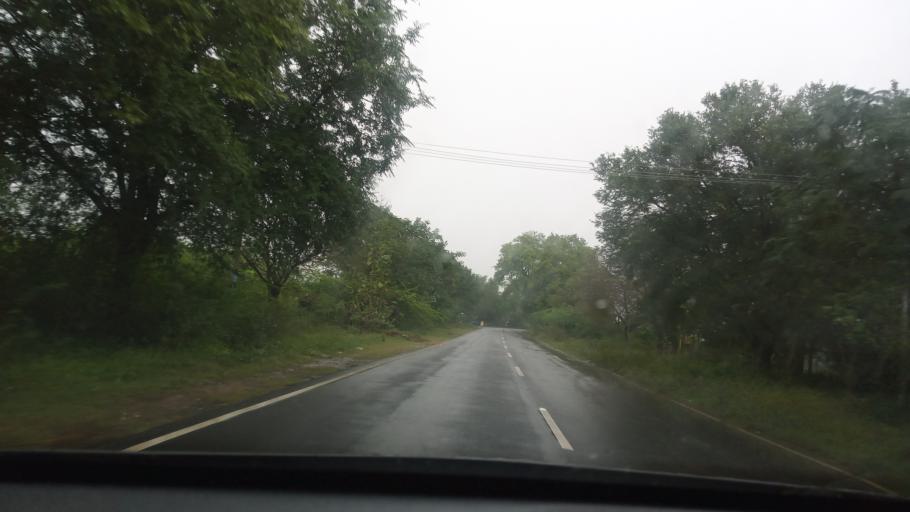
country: IN
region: Tamil Nadu
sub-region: Vellore
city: Kalavai
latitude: 12.8258
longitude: 79.4075
